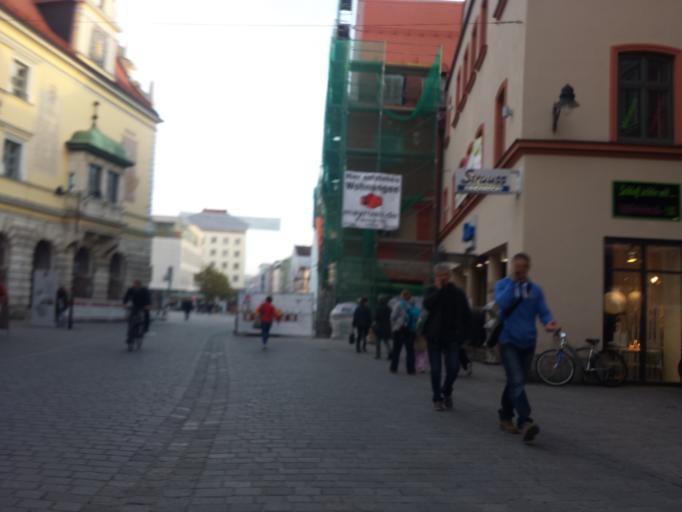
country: DE
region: Bavaria
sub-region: Upper Bavaria
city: Ingolstadt
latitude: 48.7634
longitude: 11.4244
